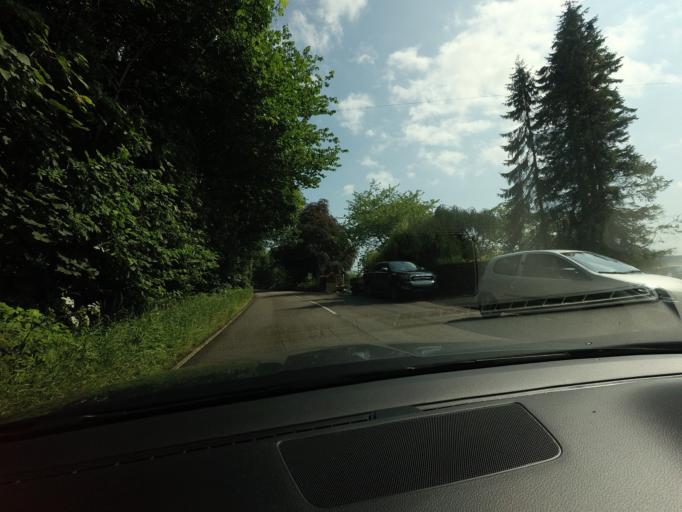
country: GB
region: Scotland
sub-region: Highland
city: Dingwall
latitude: 57.6159
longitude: -4.3962
